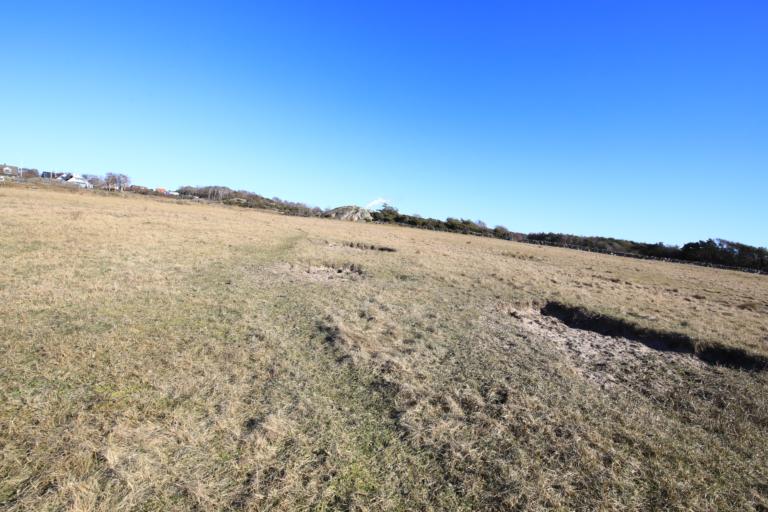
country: SE
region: Halland
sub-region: Kungsbacka Kommun
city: Frillesas
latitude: 57.2265
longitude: 12.1269
